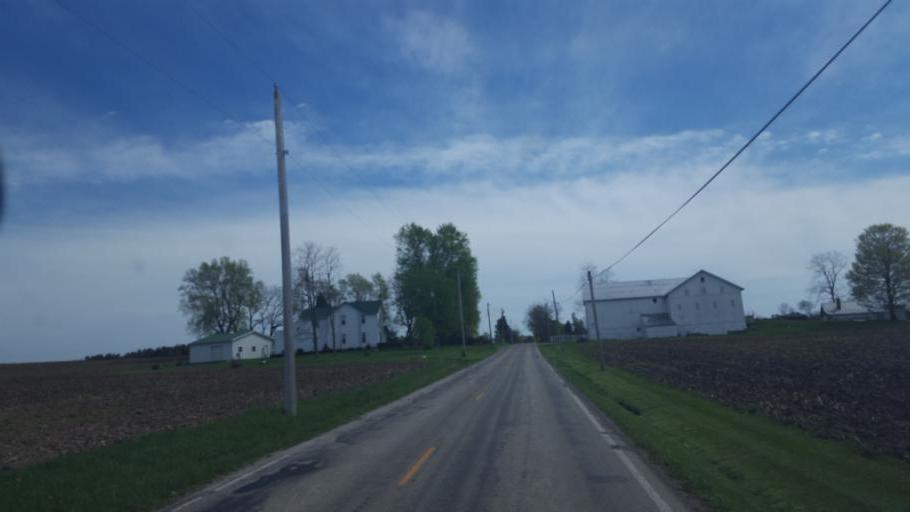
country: US
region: Ohio
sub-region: Richland County
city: Shelby
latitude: 40.8933
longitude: -82.6234
